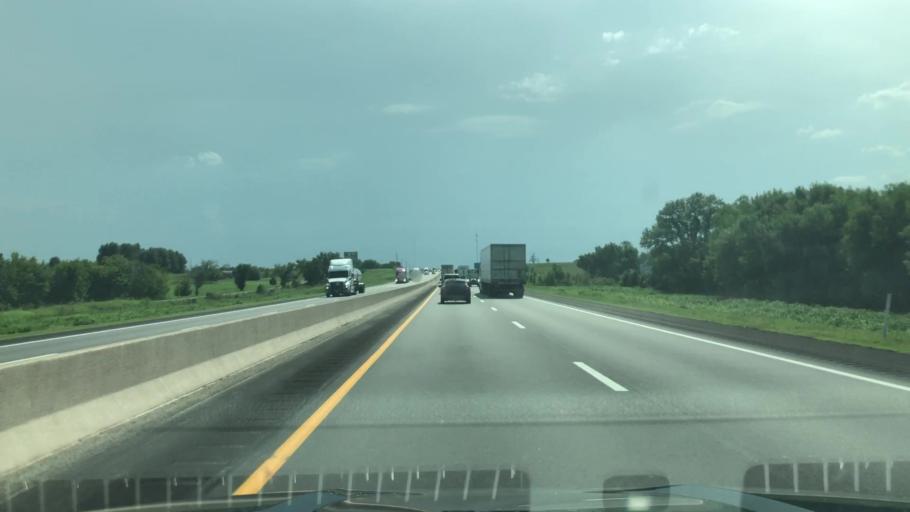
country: US
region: Oklahoma
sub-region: Craig County
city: Vinita
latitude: 36.6501
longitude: -95.1097
